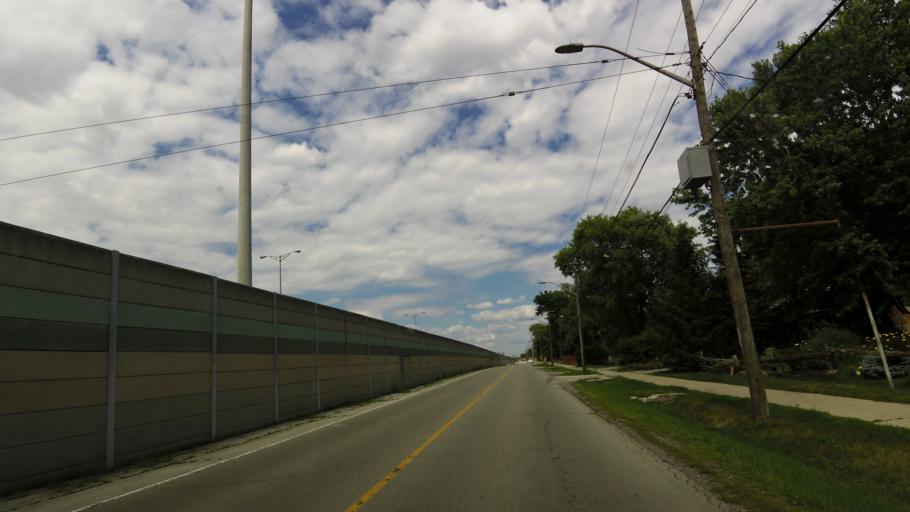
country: CA
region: Ontario
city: Mississauga
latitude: 43.5757
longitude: -79.5913
